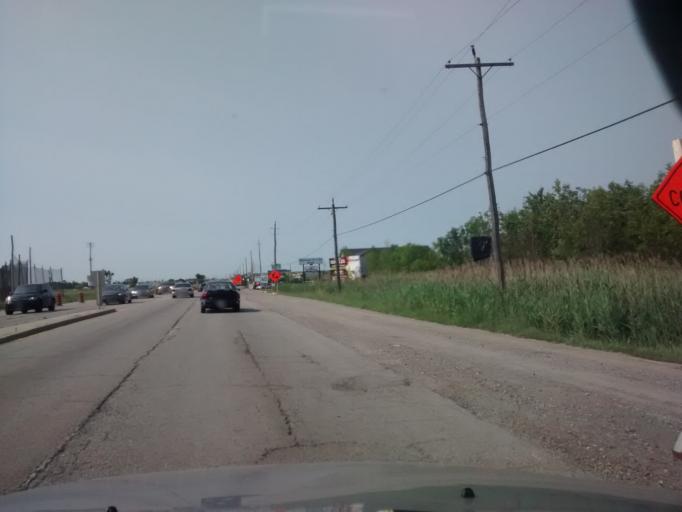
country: CA
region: Ontario
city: Hamilton
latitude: 43.1895
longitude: -79.7697
